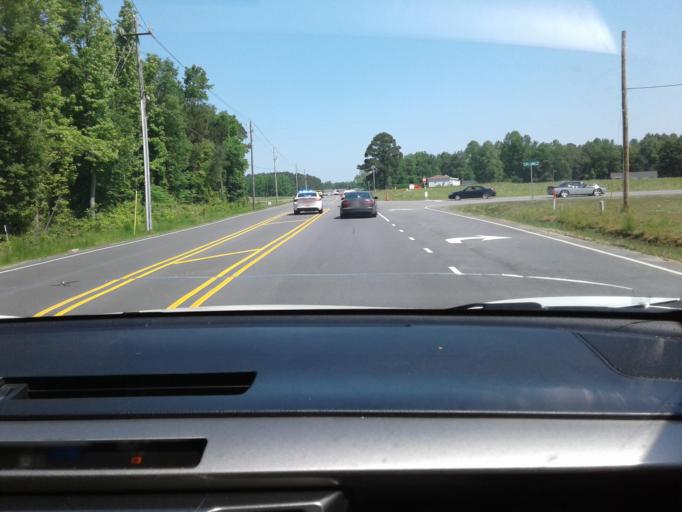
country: US
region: North Carolina
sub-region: Wake County
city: Holly Springs
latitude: 35.6174
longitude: -78.8408
